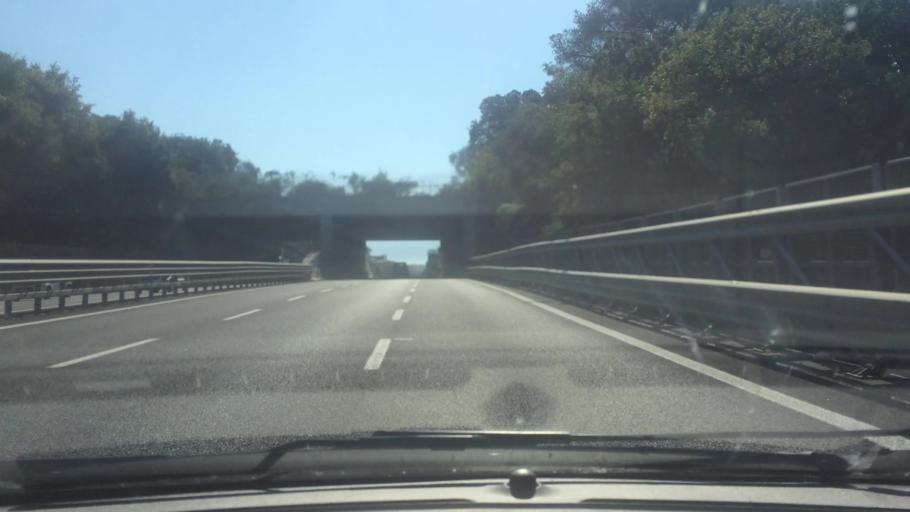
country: IT
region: Campania
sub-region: Provincia di Napoli
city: Ercolano
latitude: 40.7977
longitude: 14.3722
